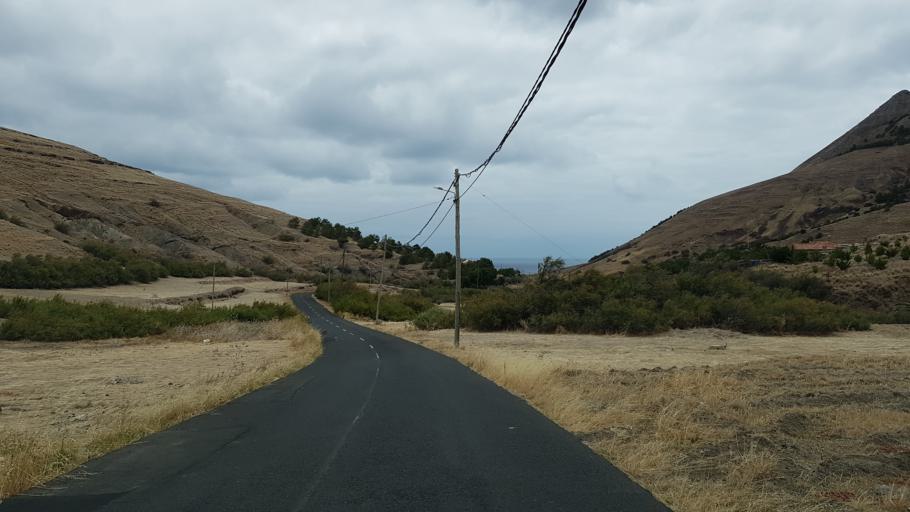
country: PT
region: Madeira
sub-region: Porto Santo
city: Vila de Porto Santo
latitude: 33.0736
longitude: -16.3117
